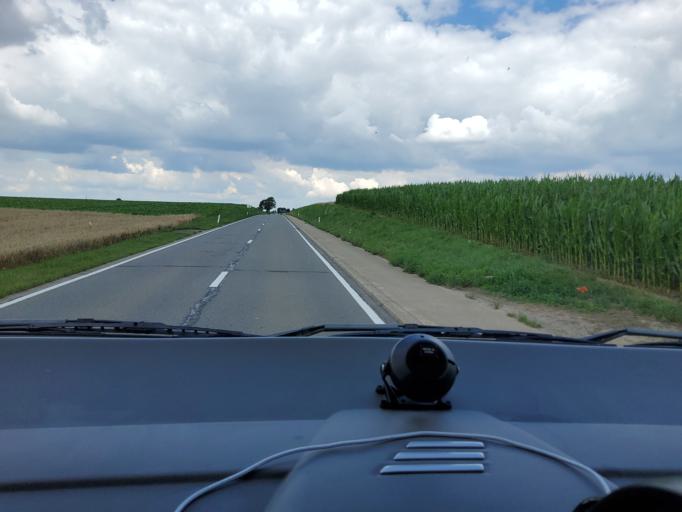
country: BE
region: Wallonia
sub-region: Province du Brabant Wallon
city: Genappe
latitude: 50.5767
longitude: 4.4347
